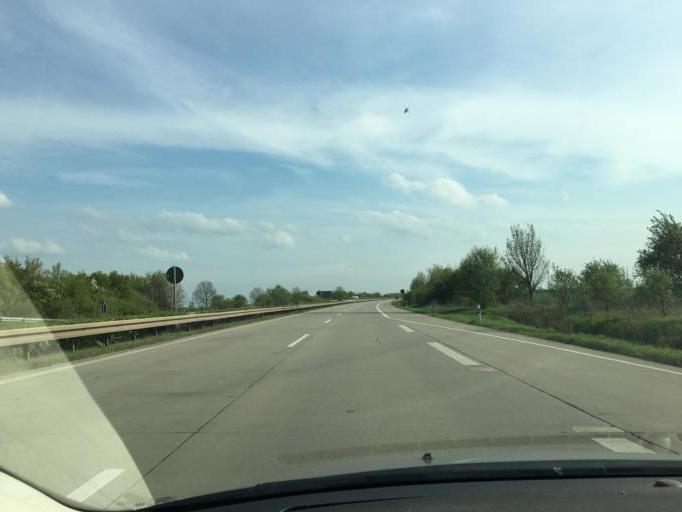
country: DE
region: Saxony-Anhalt
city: Dahlenwarsleben
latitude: 52.2001
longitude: 11.5492
